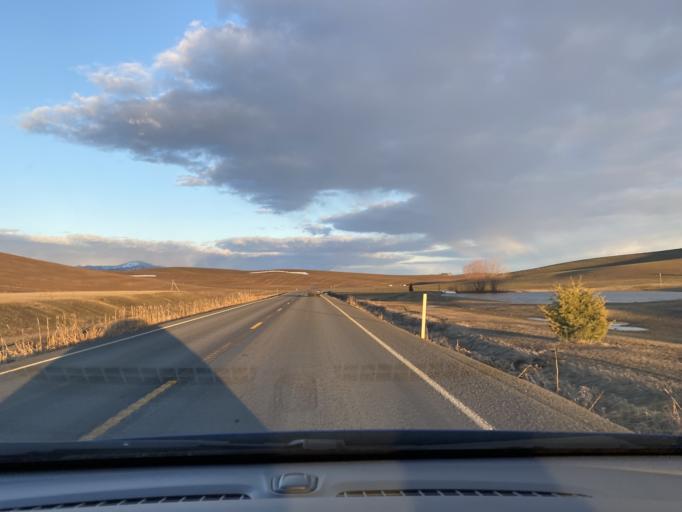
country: US
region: Idaho
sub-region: Latah County
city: Moscow
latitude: 46.7523
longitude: -117.0659
